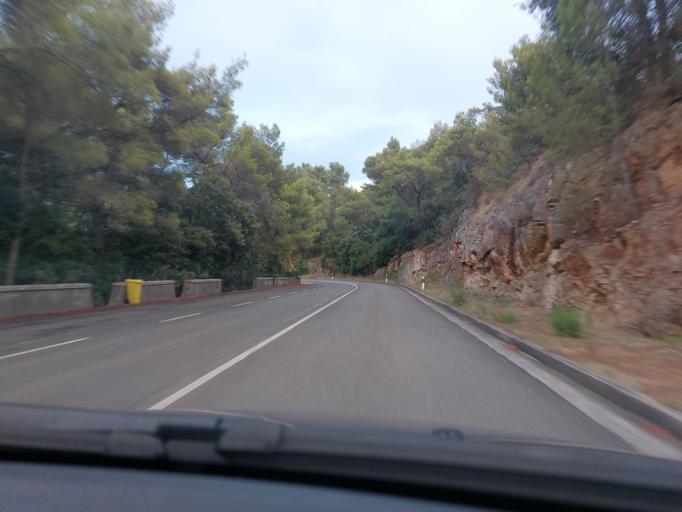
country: HR
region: Dubrovacko-Neretvanska
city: Smokvica
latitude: 42.7663
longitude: 16.8862
